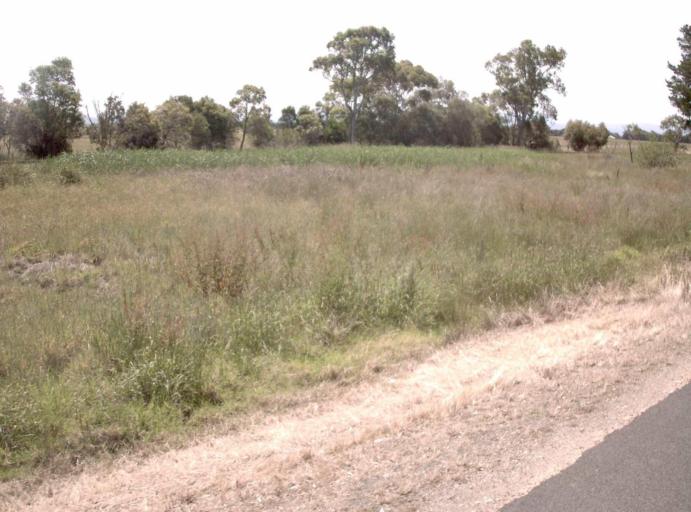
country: AU
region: Victoria
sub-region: Wellington
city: Sale
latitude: -38.0052
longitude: 147.0631
